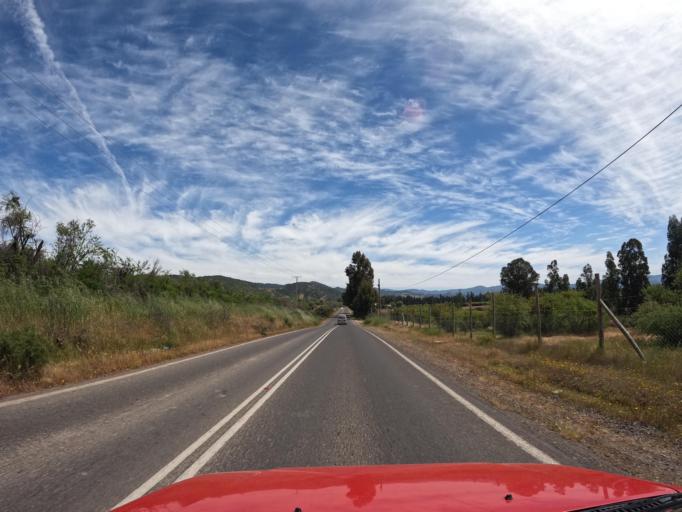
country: CL
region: Maule
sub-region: Provincia de Talca
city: Talca
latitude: -35.1128
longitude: -71.6341
